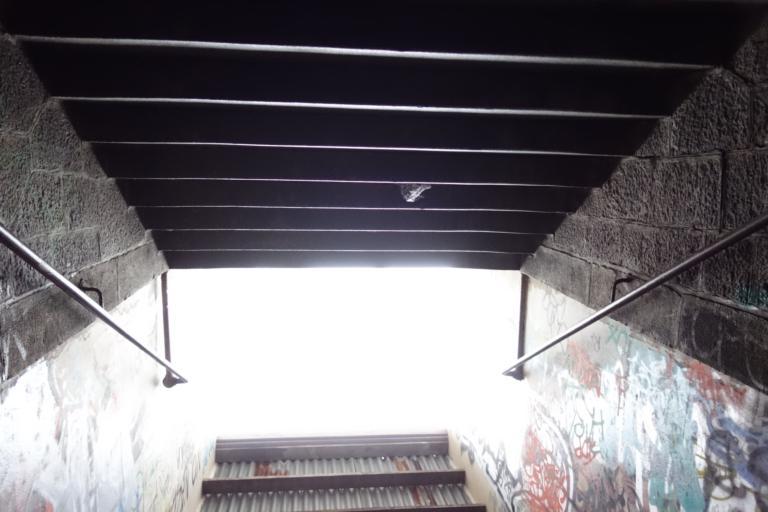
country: DE
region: Saxony
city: Freiberg
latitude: 50.9092
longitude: 13.3403
